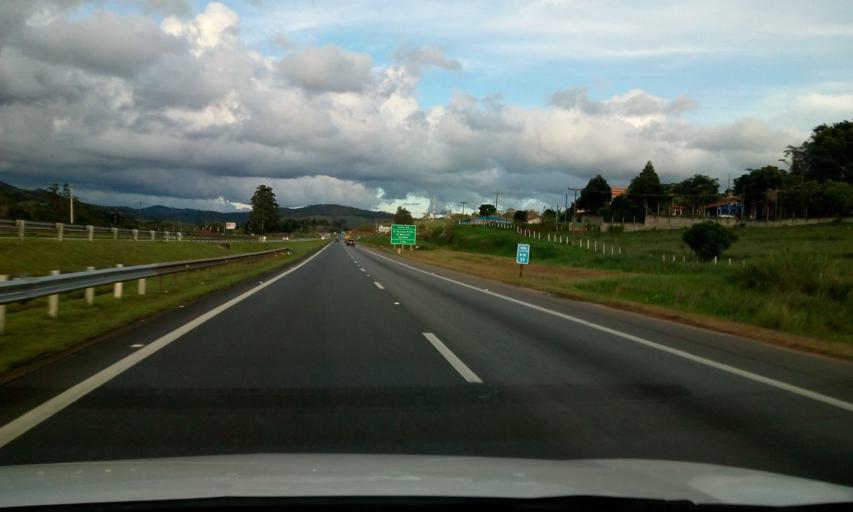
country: BR
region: Sao Paulo
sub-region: Bom Jesus Dos Perdoes
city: Bom Jesus dos Perdoes
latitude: -23.1705
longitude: -46.4206
